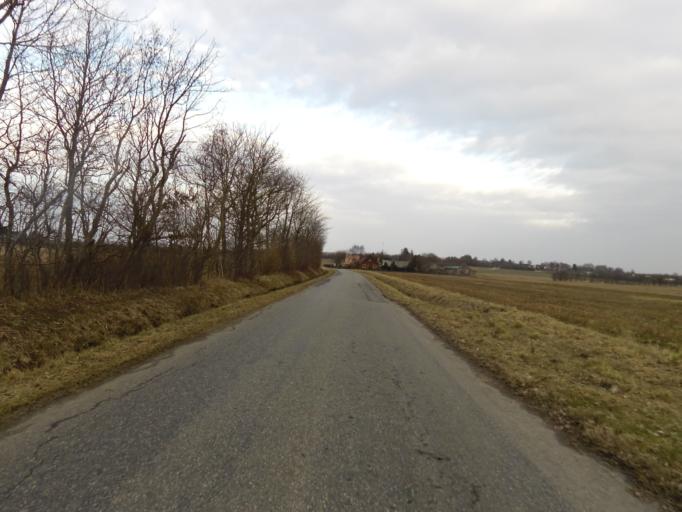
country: DK
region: South Denmark
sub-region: Tonder Kommune
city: Toftlund
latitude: 55.1810
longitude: 9.0507
